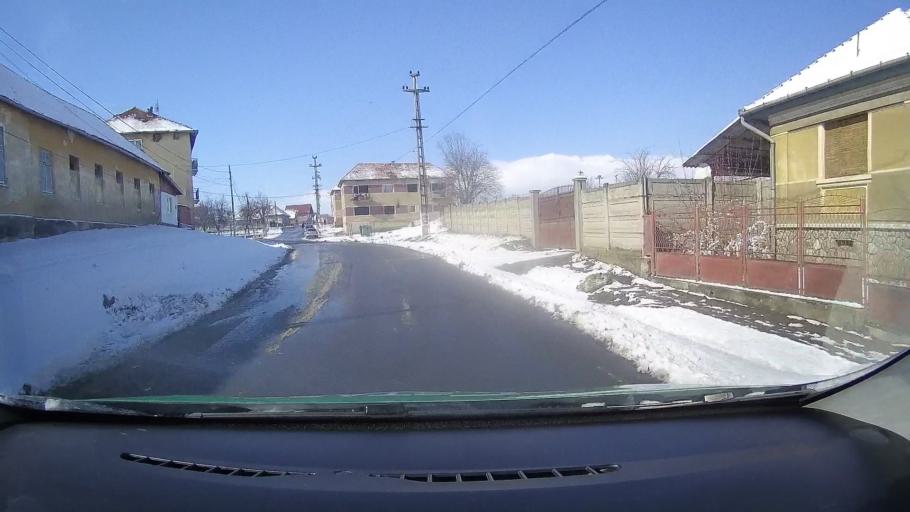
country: RO
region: Sibiu
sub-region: Comuna Rosia
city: Rosia
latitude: 45.8168
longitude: 24.3109
